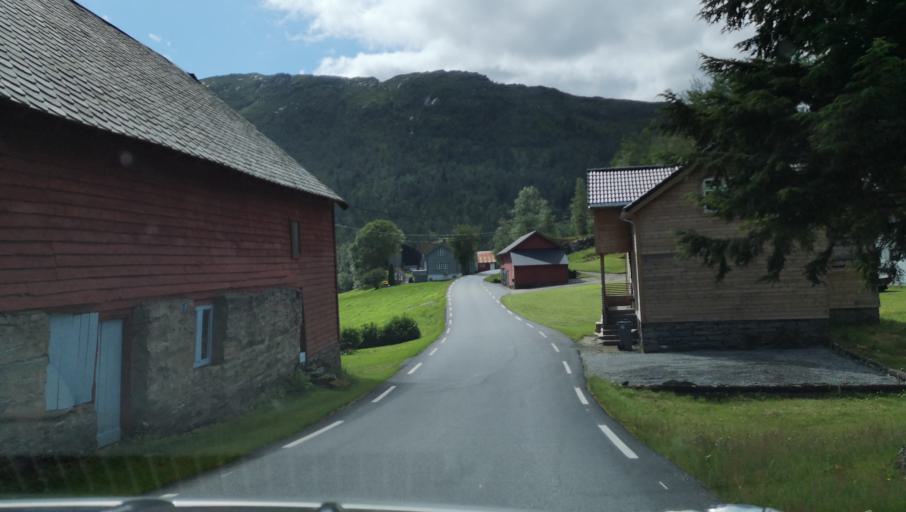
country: NO
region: Hordaland
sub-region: Modalen
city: Mo
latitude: 60.7843
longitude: 5.9239
